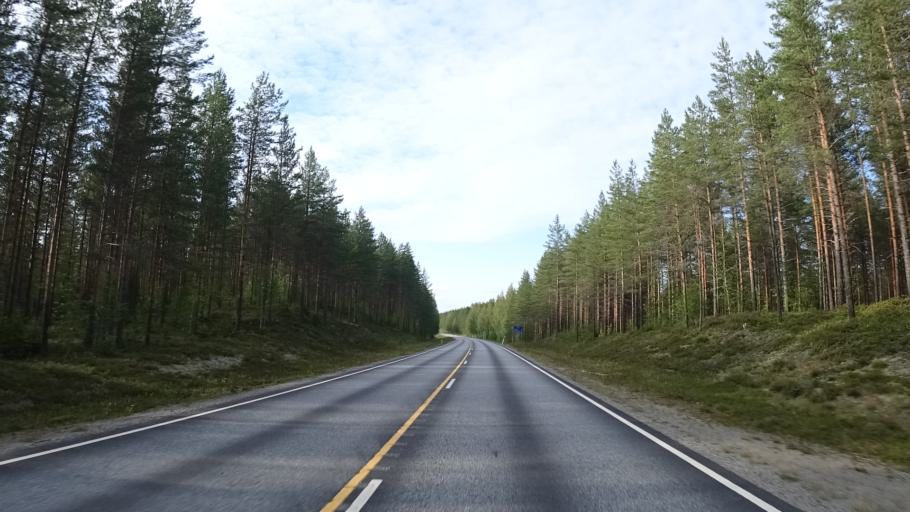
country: FI
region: North Karelia
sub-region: Joensuu
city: Eno
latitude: 62.8331
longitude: 30.1967
